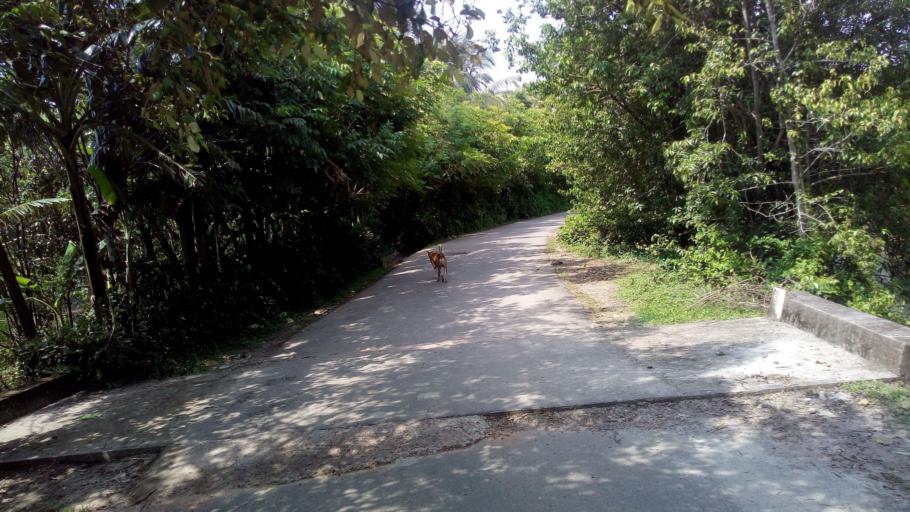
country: BD
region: Khulna
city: Phultala
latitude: 22.5749
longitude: 89.4515
